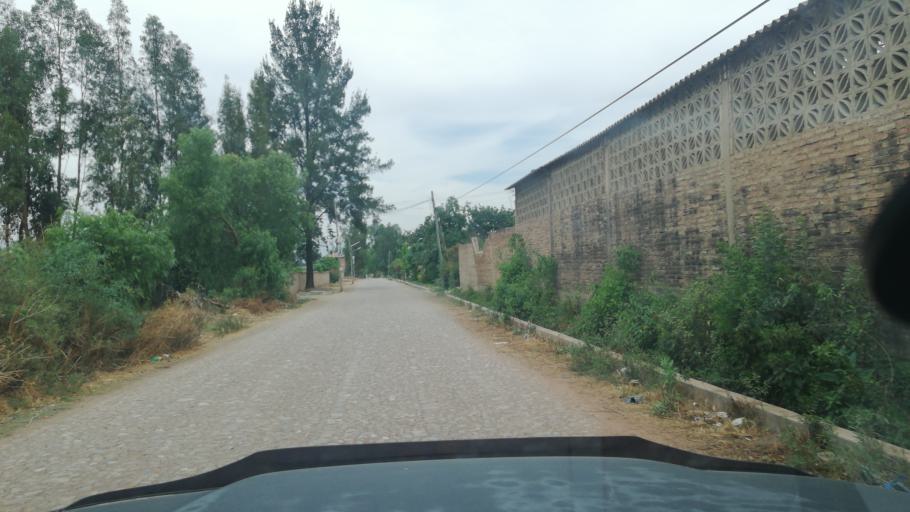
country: BO
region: Cochabamba
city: Cochabamba
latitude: -17.3574
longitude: -66.2210
